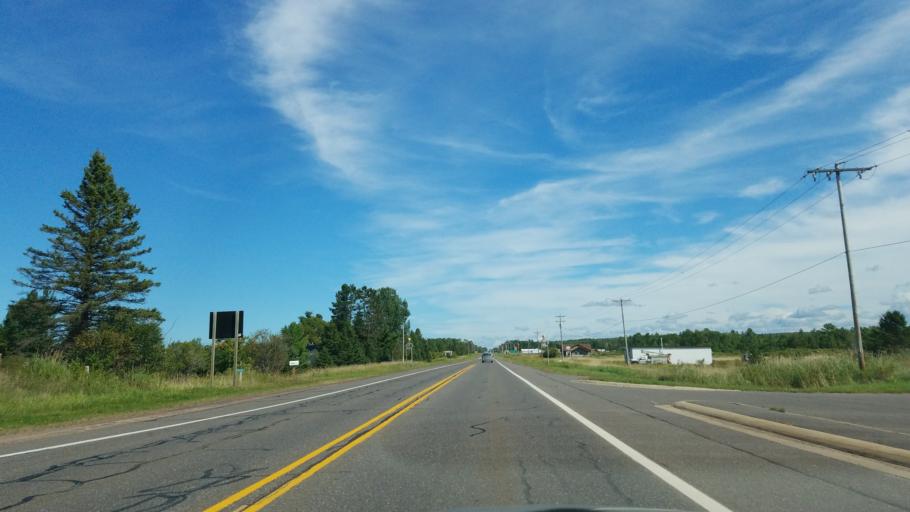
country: US
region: Michigan
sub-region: Ontonagon County
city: Ontonagon
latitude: 46.5348
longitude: -89.1756
